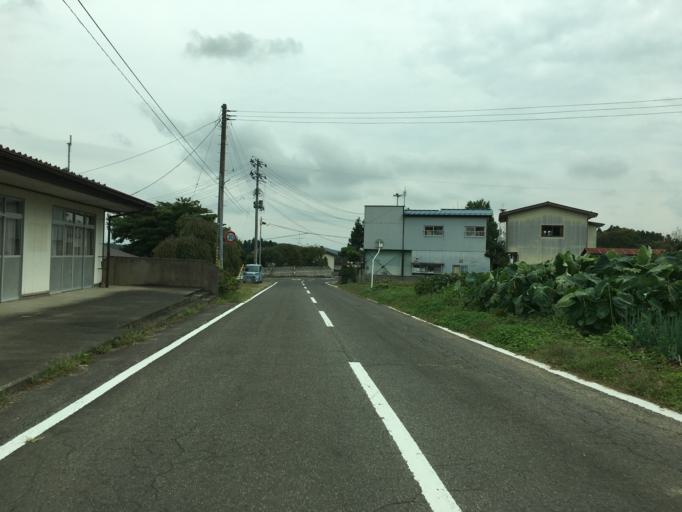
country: JP
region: Fukushima
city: Nihommatsu
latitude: 37.5841
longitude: 140.3904
